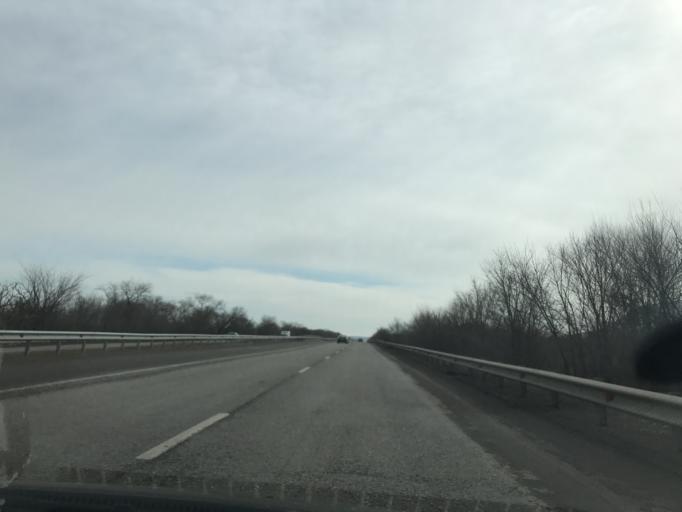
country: RU
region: Stavropol'skiy
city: Kangly
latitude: 44.2283
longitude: 43.0478
